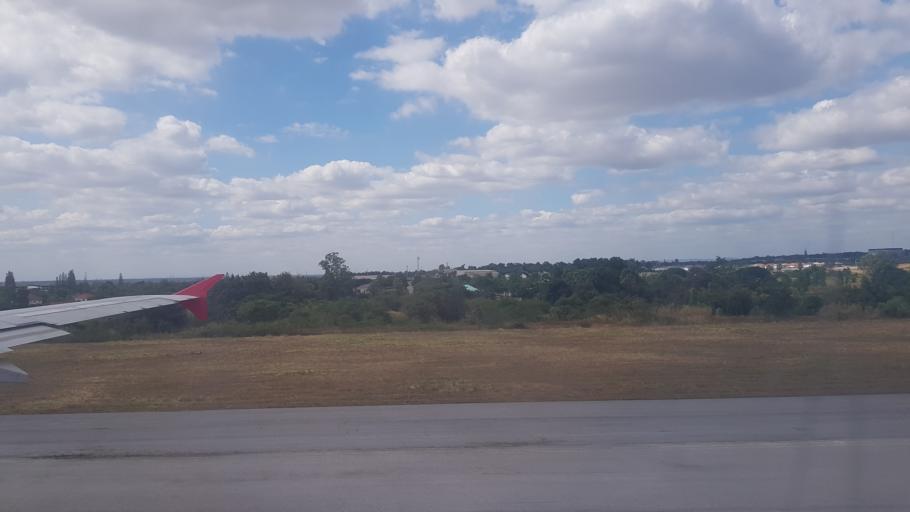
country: TH
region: Khon Kaen
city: Khon Kaen
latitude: 16.4582
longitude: 102.7782
